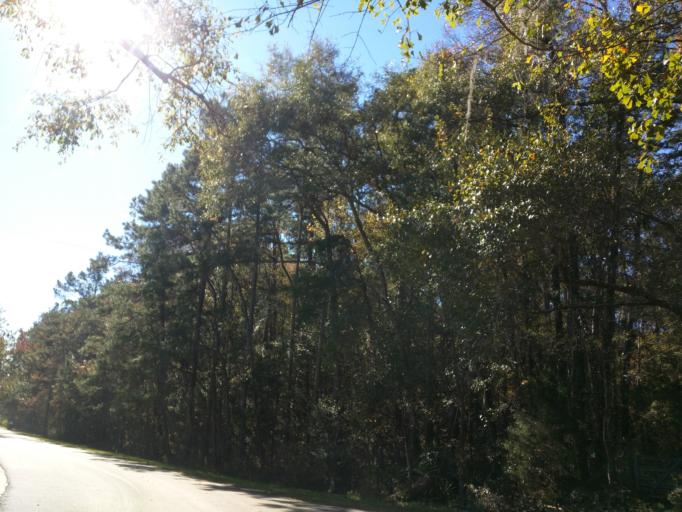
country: US
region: Florida
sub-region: Leon County
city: Tallahassee
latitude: 30.4994
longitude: -84.3131
